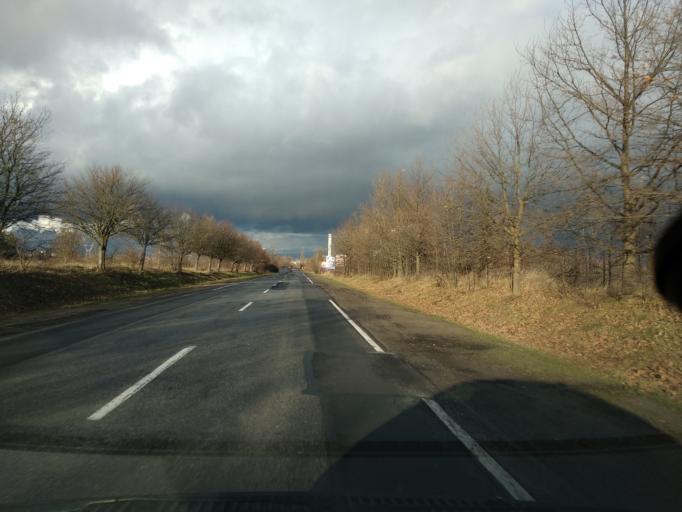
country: PL
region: Greater Poland Voivodeship
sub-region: Konin
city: Konin
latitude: 52.2705
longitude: 18.2670
